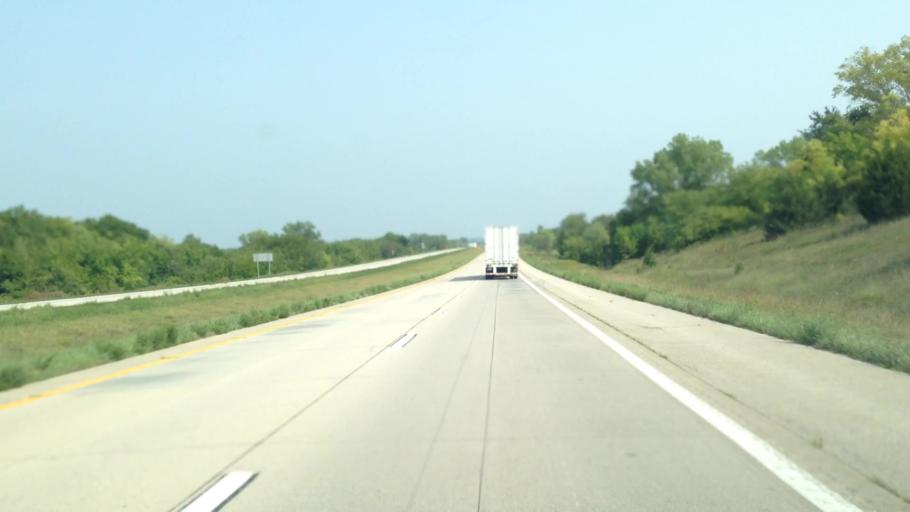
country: US
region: Missouri
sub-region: Daviess County
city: Gallatin
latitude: 39.9835
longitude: -94.0945
